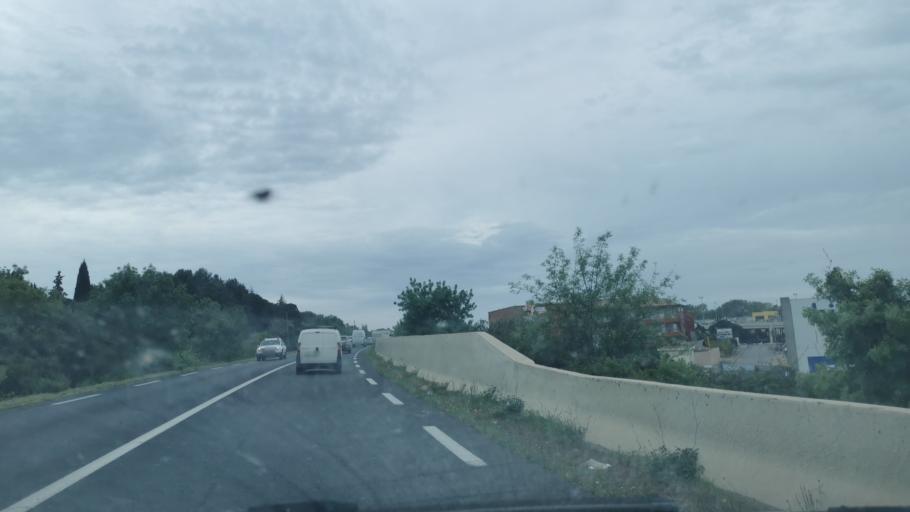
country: FR
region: Languedoc-Roussillon
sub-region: Departement de l'Herault
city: Balaruc-le-Vieux
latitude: 43.4661
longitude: 3.6922
